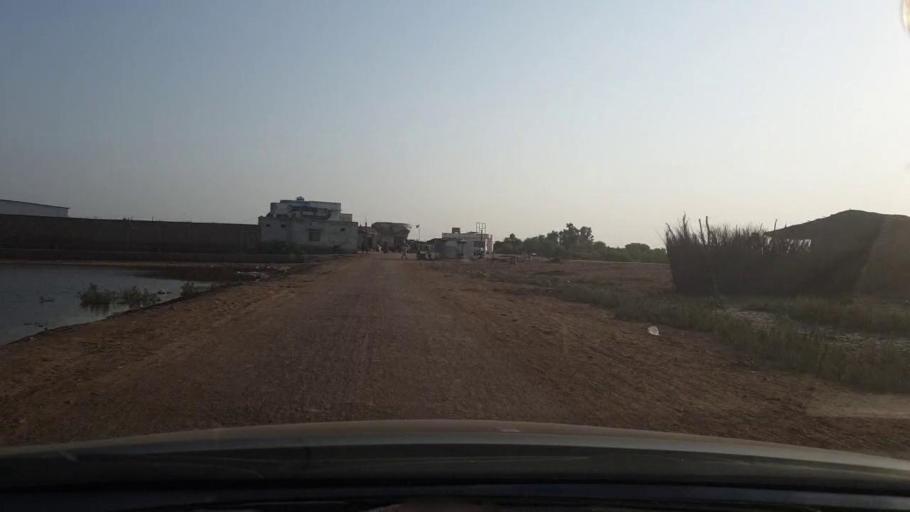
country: PK
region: Sindh
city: Naukot
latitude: 24.7558
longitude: 69.1976
